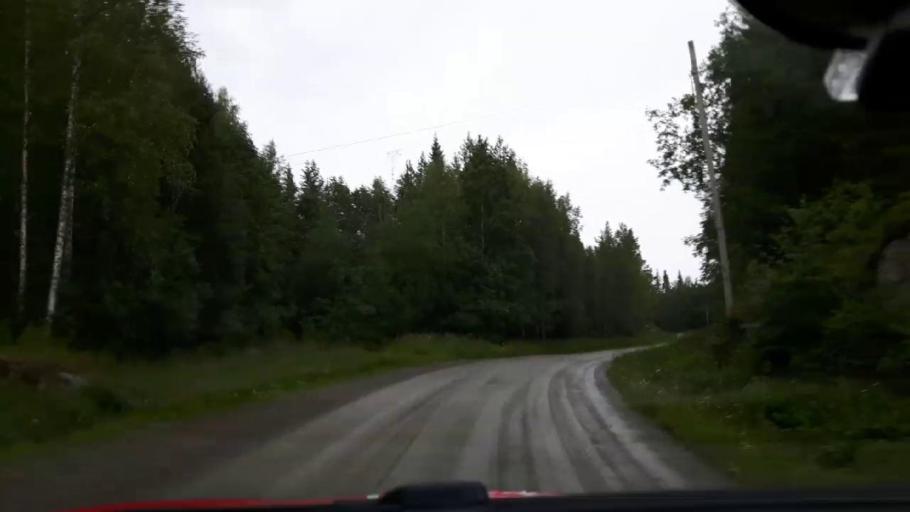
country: SE
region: Jaemtland
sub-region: OEstersunds Kommun
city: Brunflo
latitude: 62.8995
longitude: 14.8633
